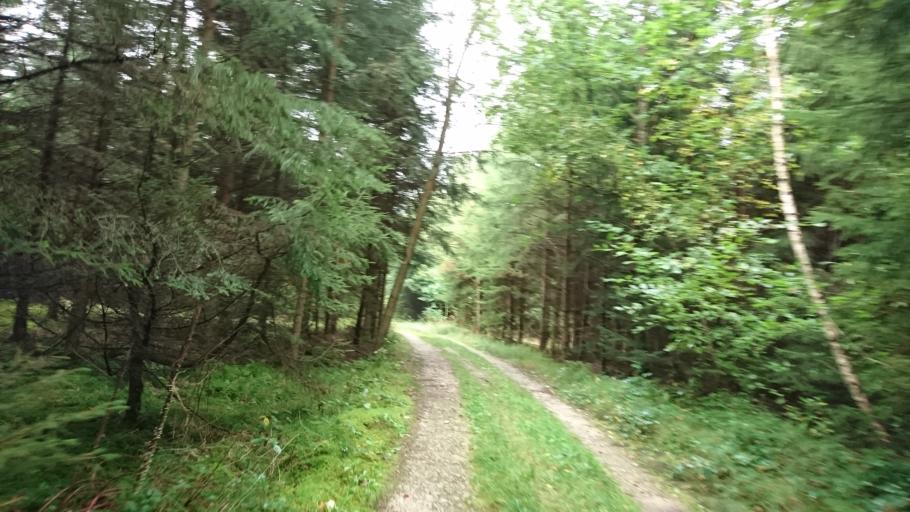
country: DE
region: Bavaria
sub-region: Swabia
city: Welden
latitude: 48.4499
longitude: 10.6489
